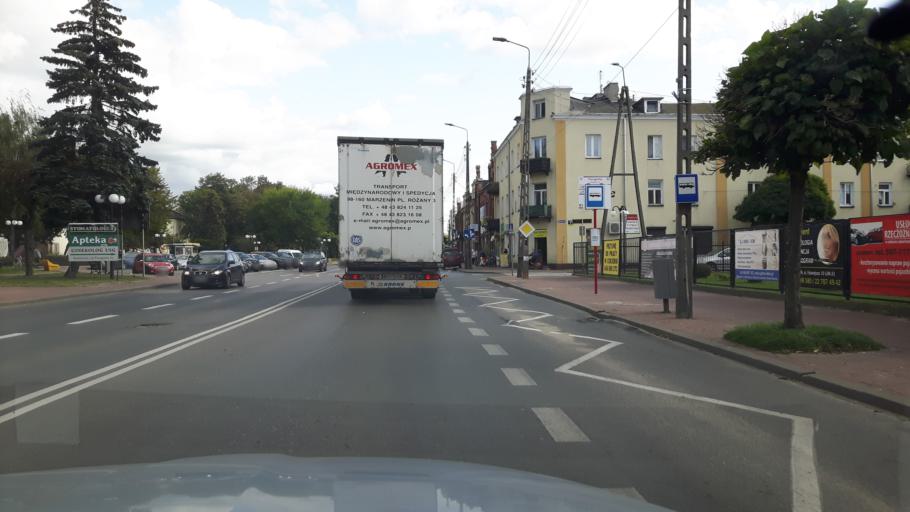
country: PL
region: Masovian Voivodeship
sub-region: Powiat wolominski
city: Radzymin
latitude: 52.4173
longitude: 21.1809
